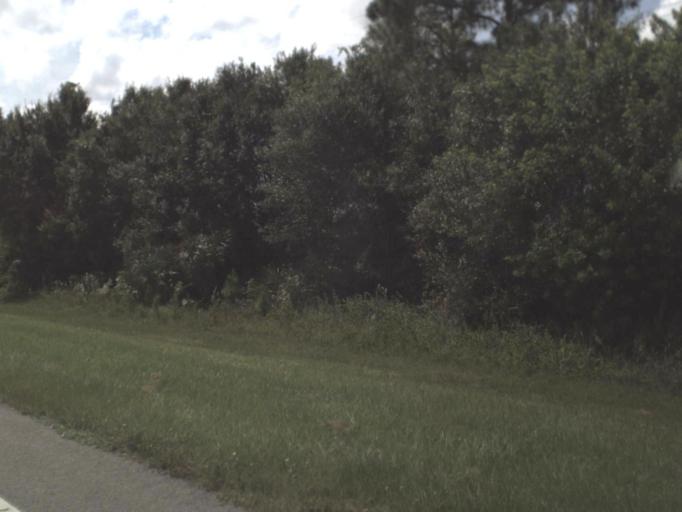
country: US
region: Florida
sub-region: Collier County
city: Immokalee
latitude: 26.3429
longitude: -81.3435
